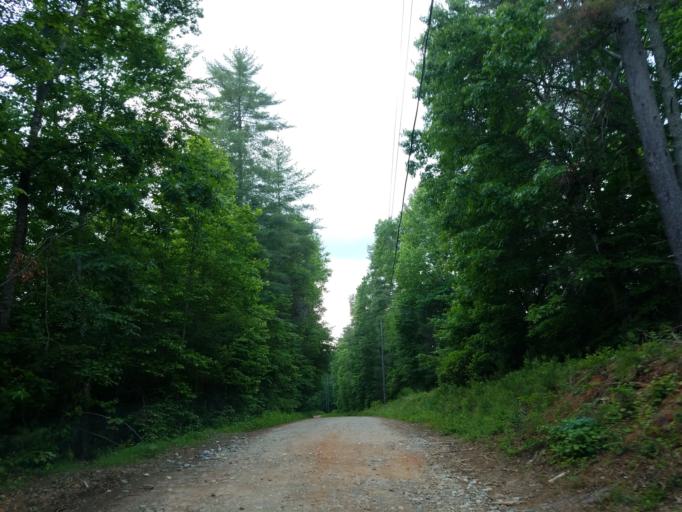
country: US
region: Georgia
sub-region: Lumpkin County
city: Dahlonega
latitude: 34.5984
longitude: -84.0860
